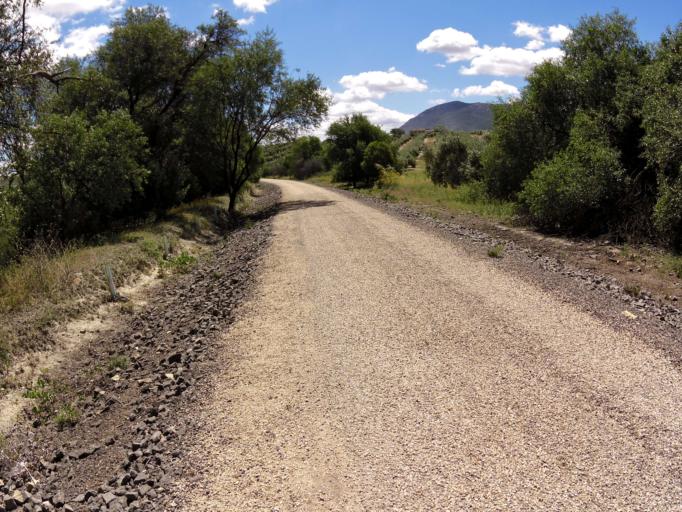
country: ES
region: Andalusia
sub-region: Provincia de Jaen
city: Alcaudete
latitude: 37.6636
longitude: -4.0496
